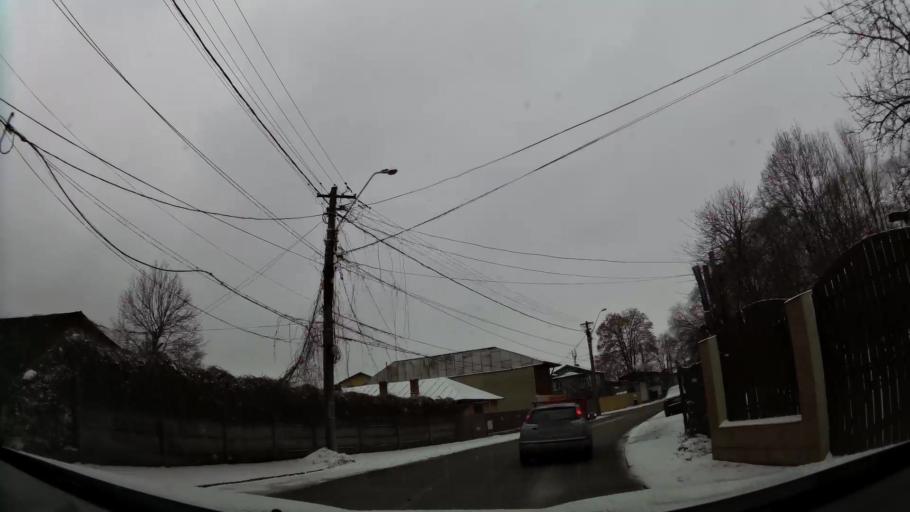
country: RO
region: Prahova
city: Ploiesti
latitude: 44.9293
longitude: 26.0151
